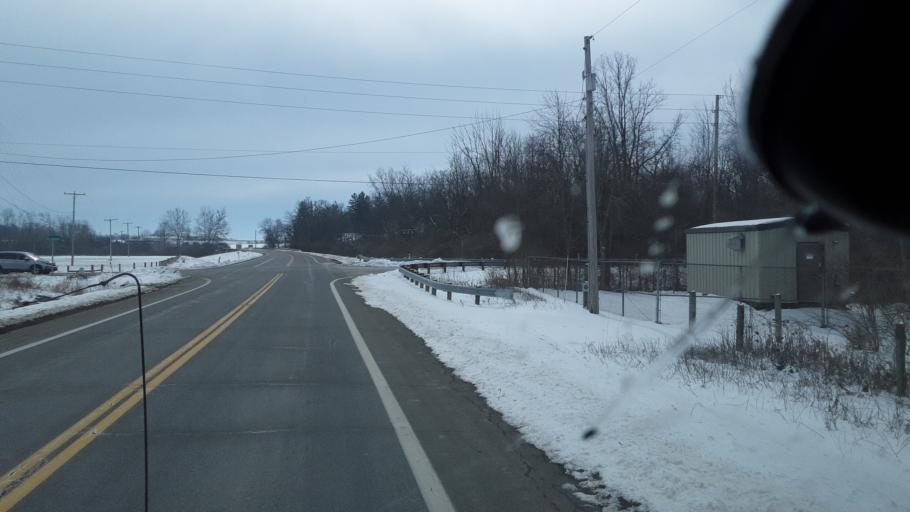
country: US
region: Ohio
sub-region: Madison County
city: Choctaw Lake
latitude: 39.9485
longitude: -83.5033
